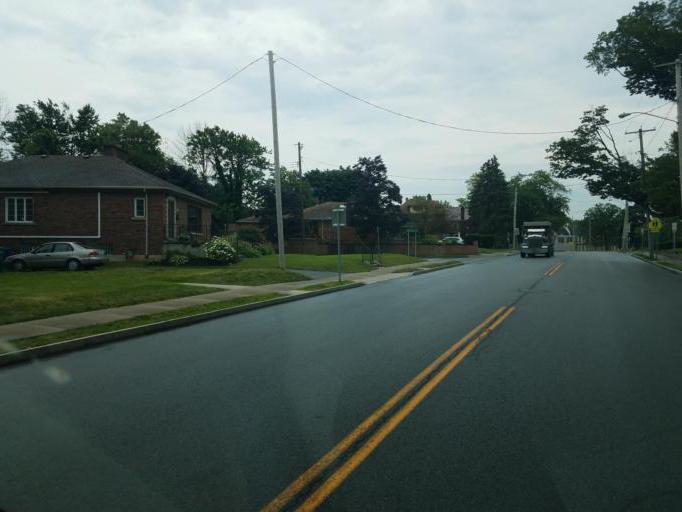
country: CA
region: Ontario
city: Niagara Falls
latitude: 43.1279
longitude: -79.0495
